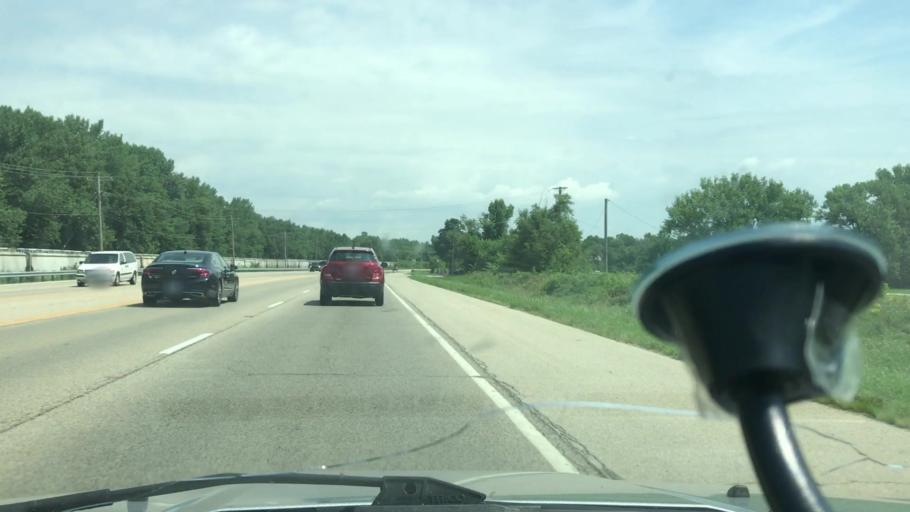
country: US
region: Illinois
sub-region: Tazewell County
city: North Pekin
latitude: 40.6080
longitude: -89.6350
